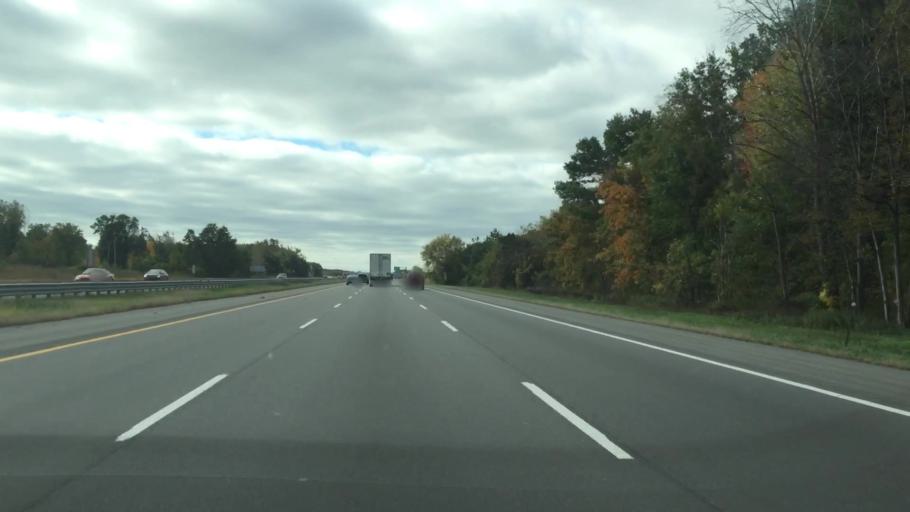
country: US
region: Michigan
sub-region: Macomb County
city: Mount Clemens
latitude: 42.6548
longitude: -82.8350
